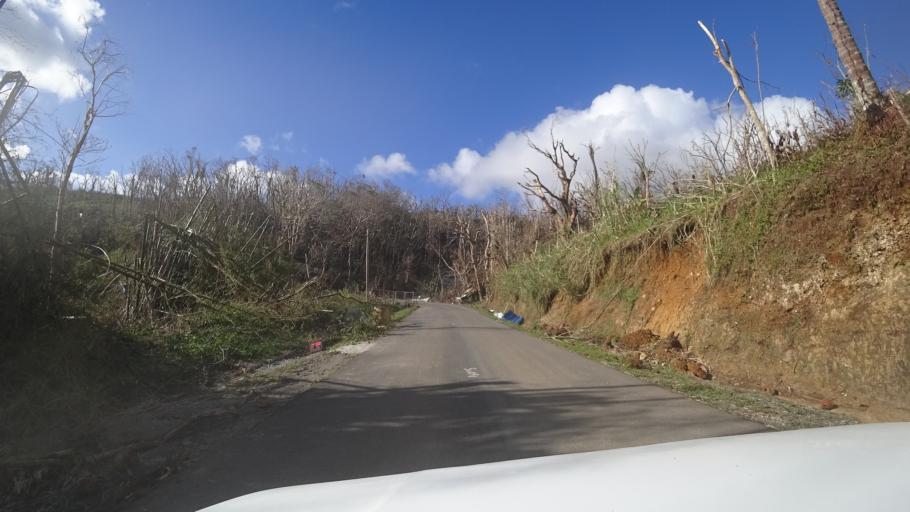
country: DM
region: Saint Luke
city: Pointe Michel
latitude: 15.2683
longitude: -61.3425
